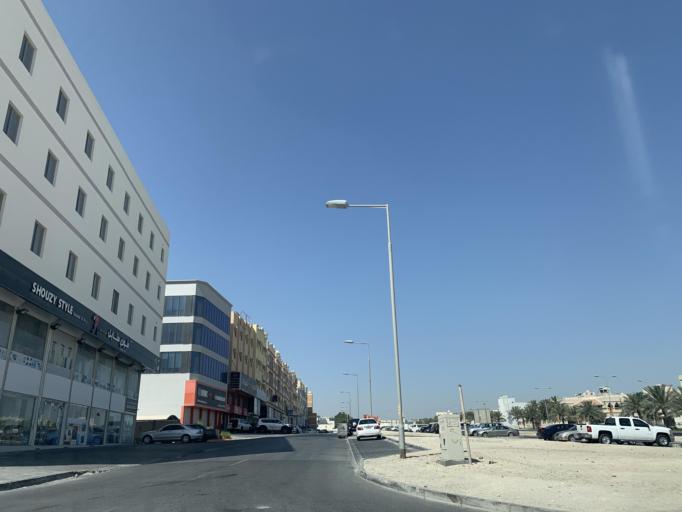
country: BH
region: Northern
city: Ar Rifa'
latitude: 26.1394
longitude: 50.5785
